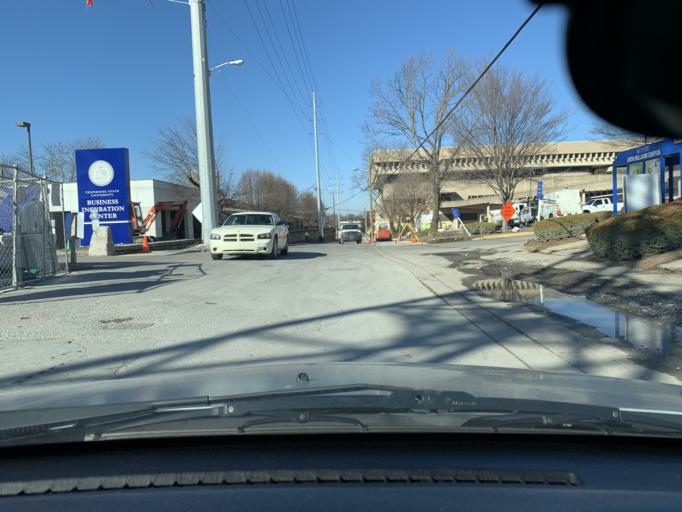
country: US
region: Tennessee
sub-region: Davidson County
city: Nashville
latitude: 36.1618
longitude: -86.7867
